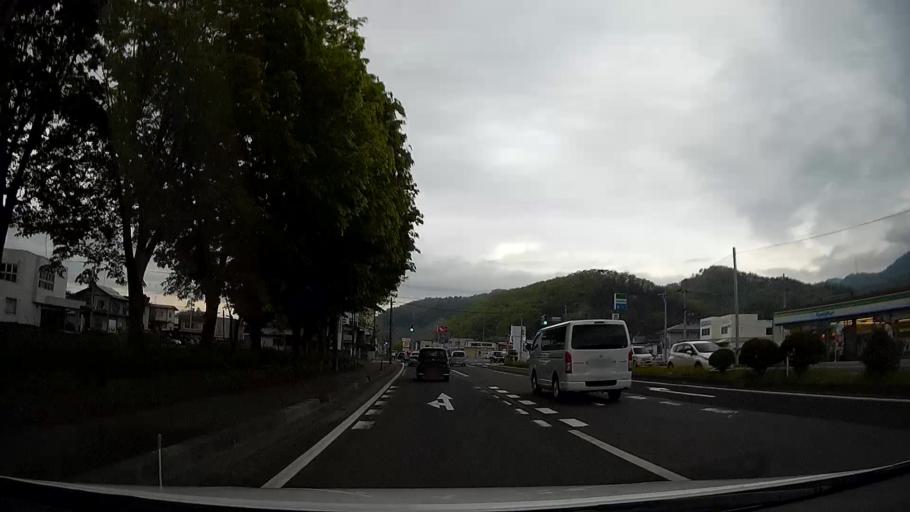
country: JP
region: Yamagata
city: Yamagata-shi
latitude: 38.2643
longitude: 140.3620
